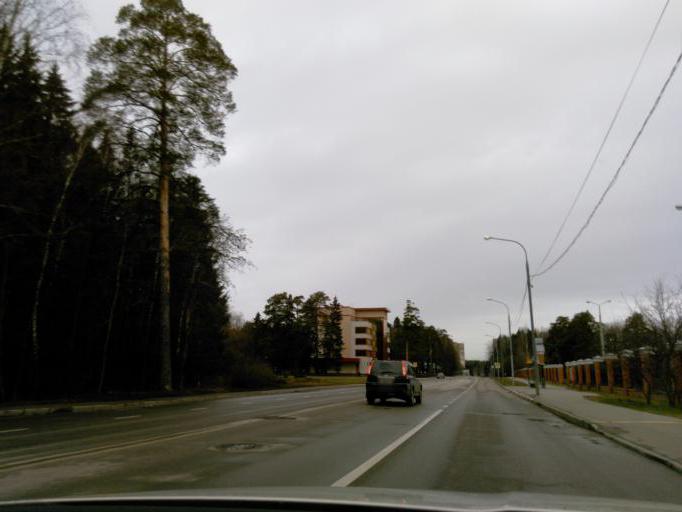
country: RU
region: Moskovskaya
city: Rzhavki
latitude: 55.9940
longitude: 37.2442
